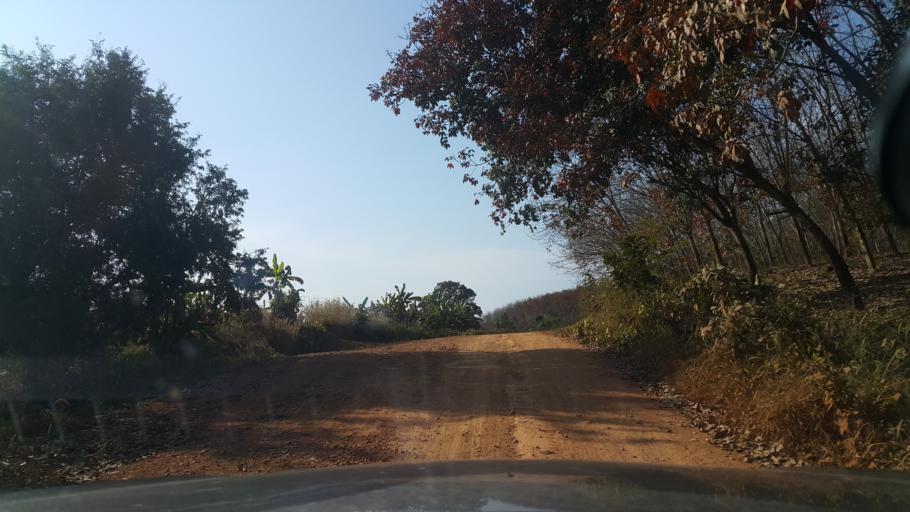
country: TH
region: Loei
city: Chiang Khan
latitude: 17.8205
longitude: 101.6171
